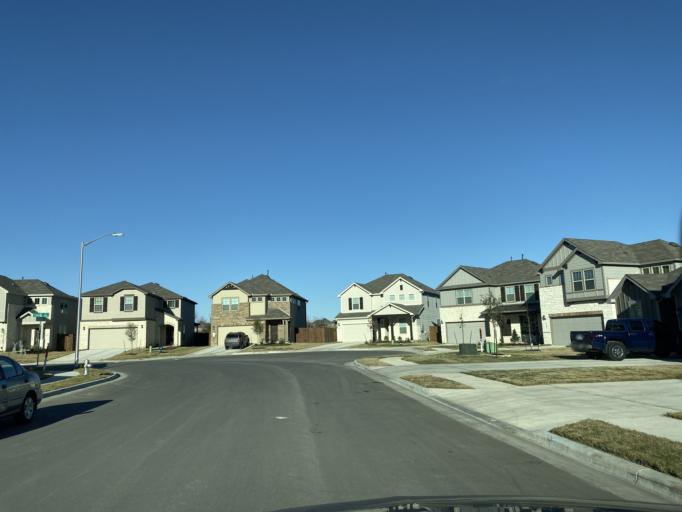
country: US
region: Texas
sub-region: Travis County
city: Wells Branch
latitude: 30.4644
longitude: -97.6763
